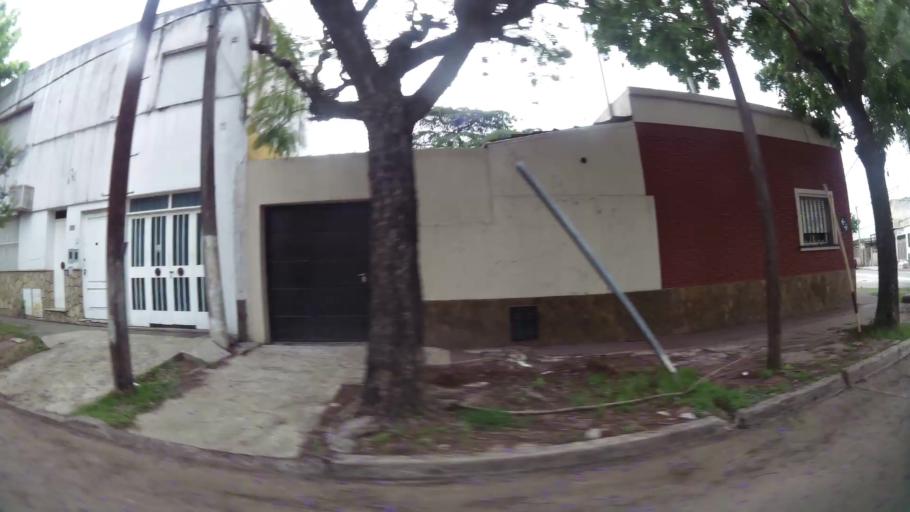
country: AR
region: Santa Fe
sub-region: Departamento de Rosario
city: Rosario
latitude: -32.9127
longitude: -60.6893
